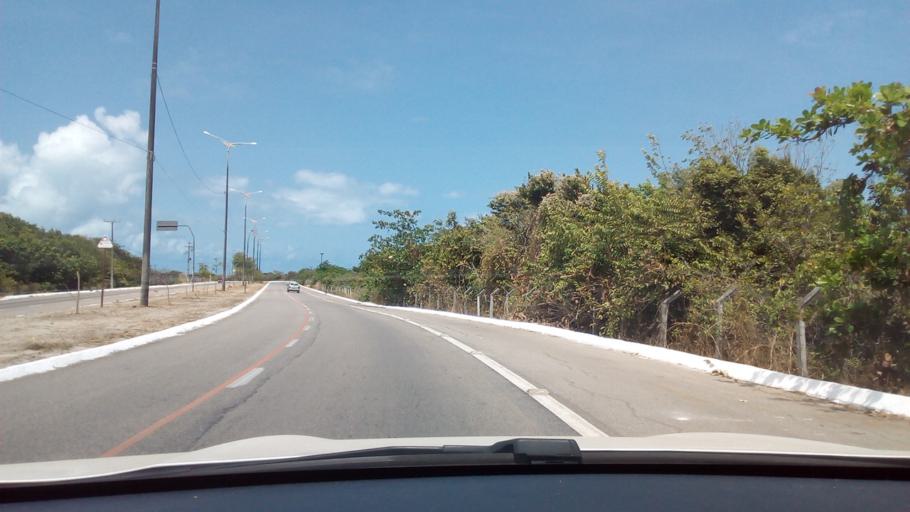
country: BR
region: Paraiba
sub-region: Joao Pessoa
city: Joao Pessoa
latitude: -7.1562
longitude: -34.7974
